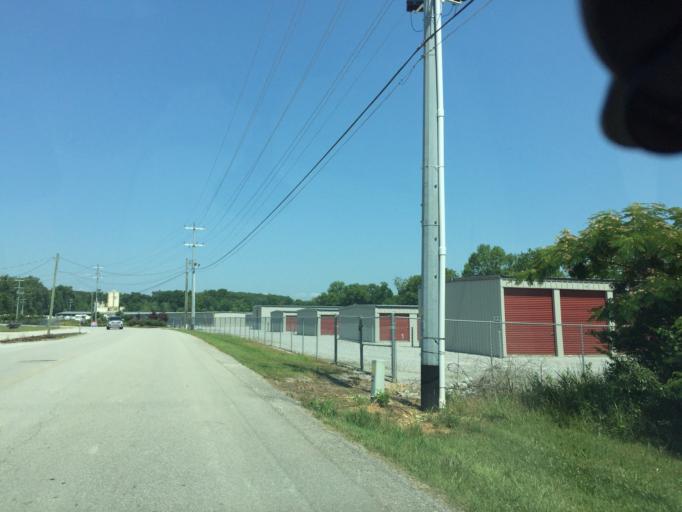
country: US
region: Tennessee
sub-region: Hamilton County
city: Collegedale
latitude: 35.0774
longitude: -85.0620
